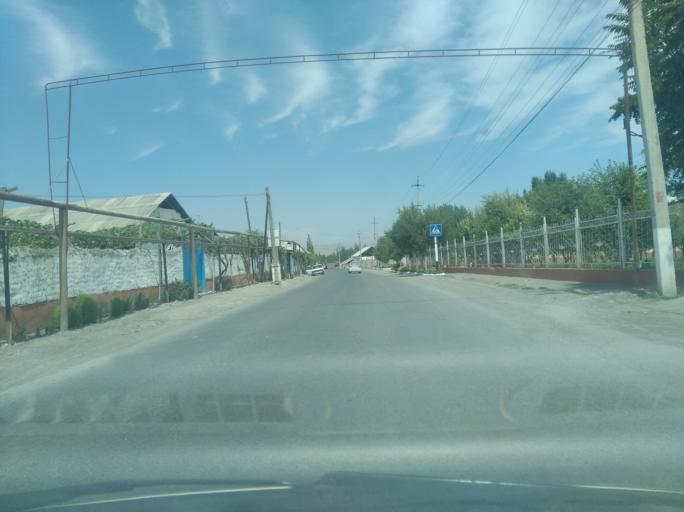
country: KG
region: Osh
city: Aravan
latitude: 40.6195
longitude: 72.4531
